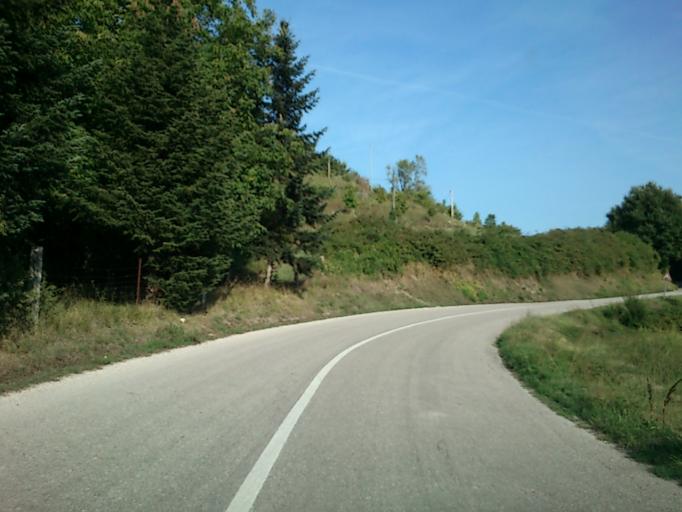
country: IT
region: The Marches
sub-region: Provincia di Pesaro e Urbino
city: Canavaccio
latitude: 43.6838
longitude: 12.7279
